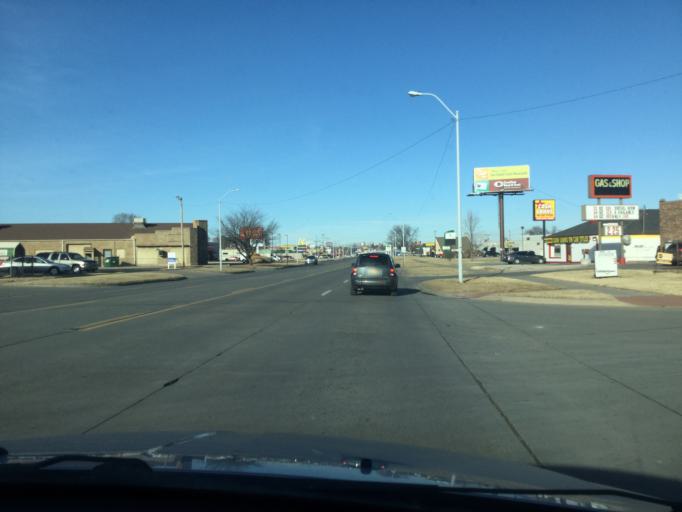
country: US
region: Kansas
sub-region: Shawnee County
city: Topeka
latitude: 39.0822
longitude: -95.6665
